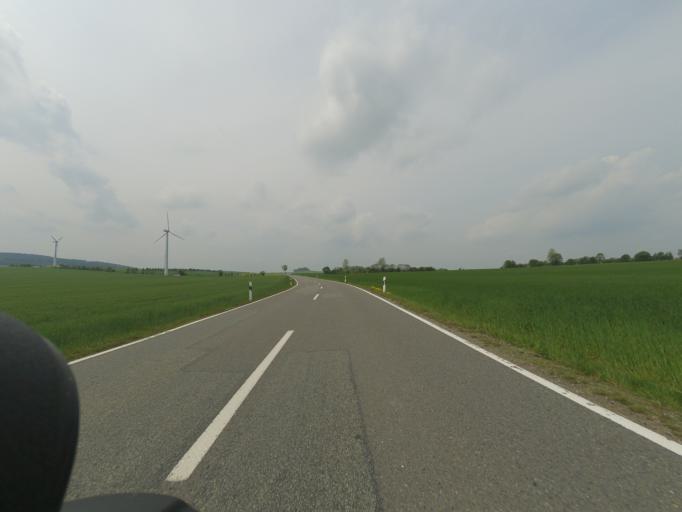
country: DE
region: Saxony
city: Zoblitz
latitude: 50.6494
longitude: 13.2710
